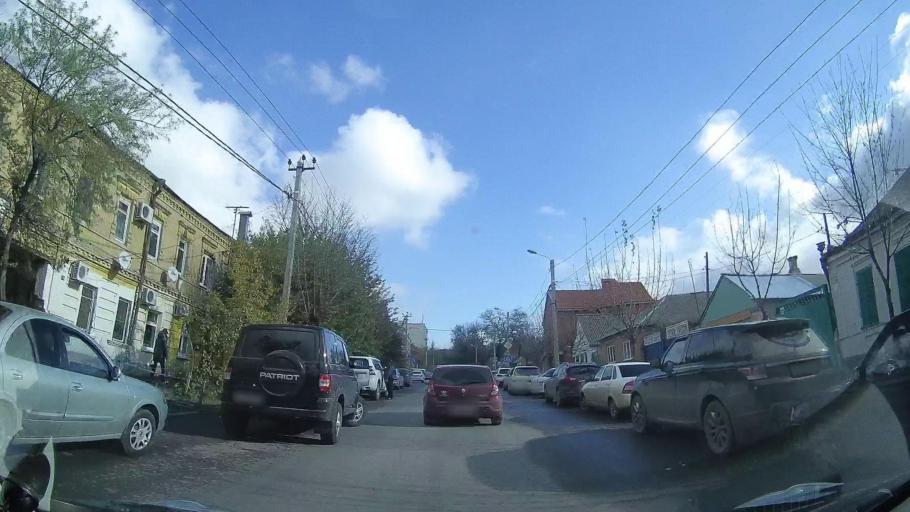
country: RU
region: Rostov
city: Rostov-na-Donu
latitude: 47.2278
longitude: 39.6875
